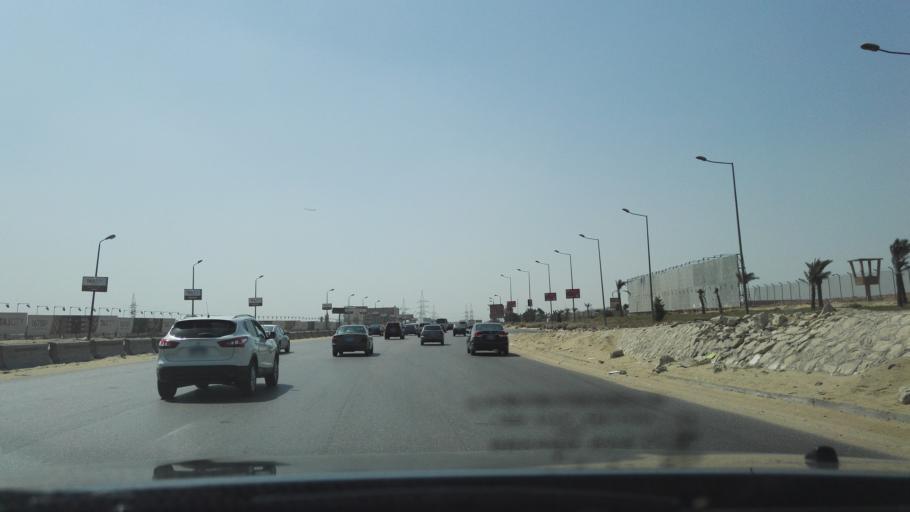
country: EG
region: Muhafazat al Qalyubiyah
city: Al Khankah
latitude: 30.0791
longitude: 31.4235
